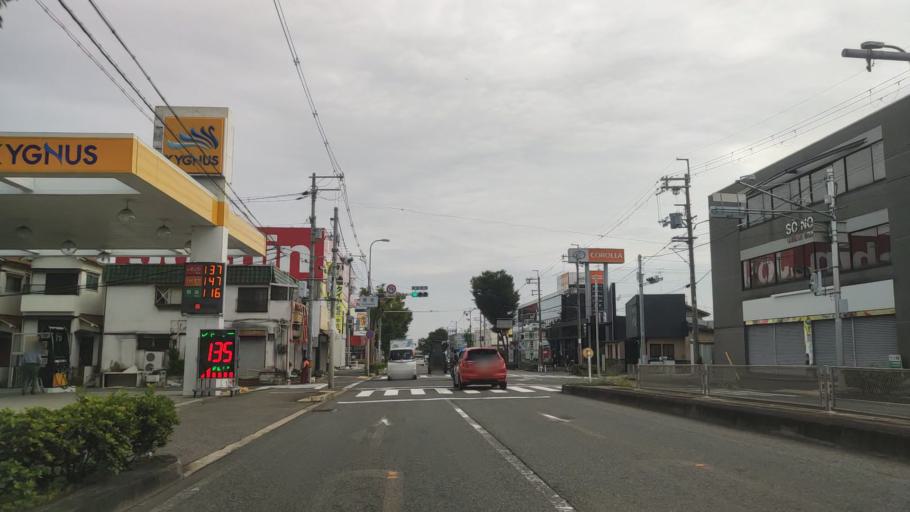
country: JP
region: Osaka
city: Tondabayashicho
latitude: 34.4504
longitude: 135.5584
